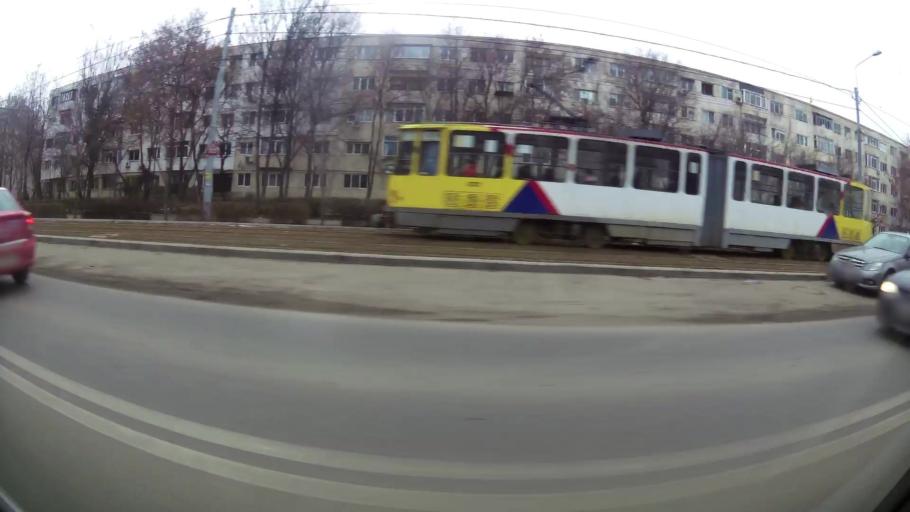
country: RO
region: Prahova
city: Ploiesti
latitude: 44.9297
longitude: 26.0322
